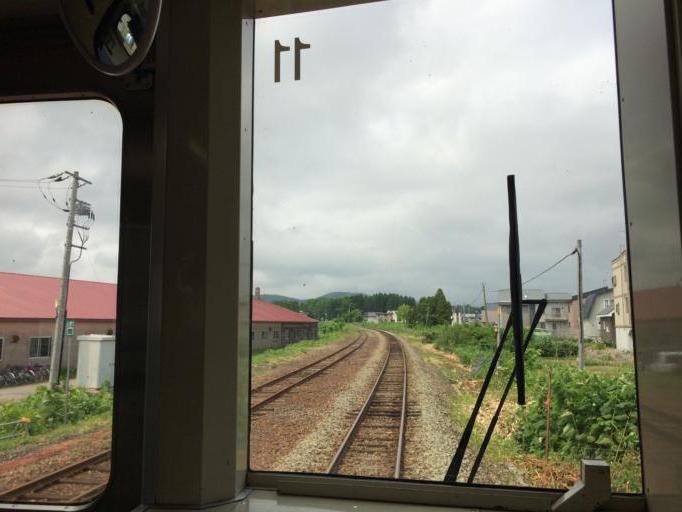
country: JP
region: Hokkaido
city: Niseko Town
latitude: 42.9057
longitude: 140.7457
